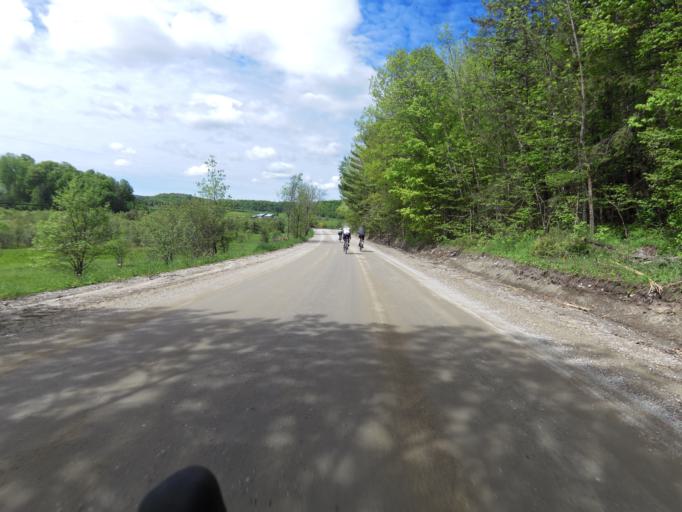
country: CA
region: Quebec
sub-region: Outaouais
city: Wakefield
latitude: 45.7834
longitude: -75.9966
